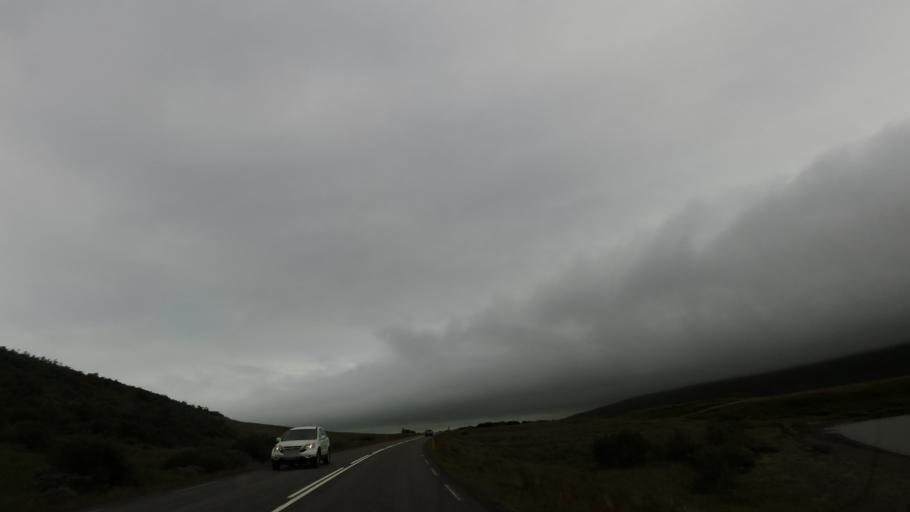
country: IS
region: Northeast
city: Laugar
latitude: 65.7090
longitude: -17.6806
